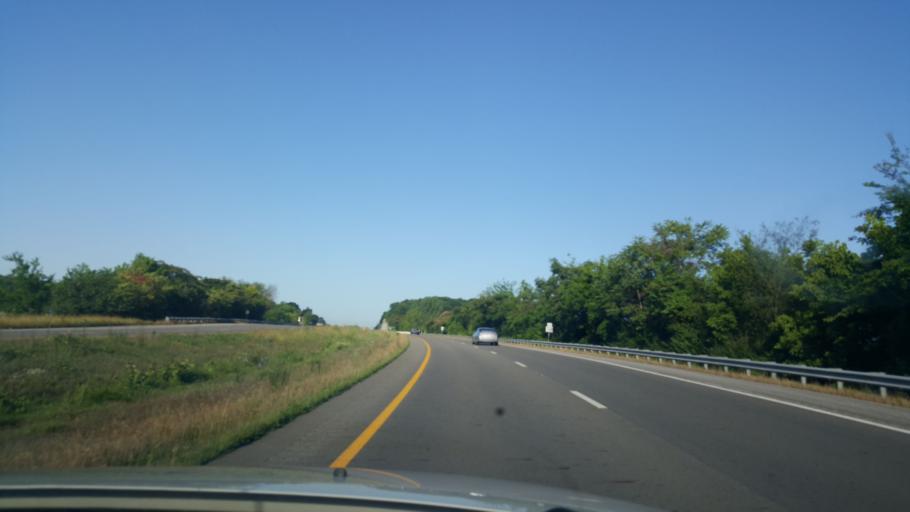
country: US
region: Tennessee
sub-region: Maury County
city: Columbia
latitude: 35.6301
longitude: -87.1017
